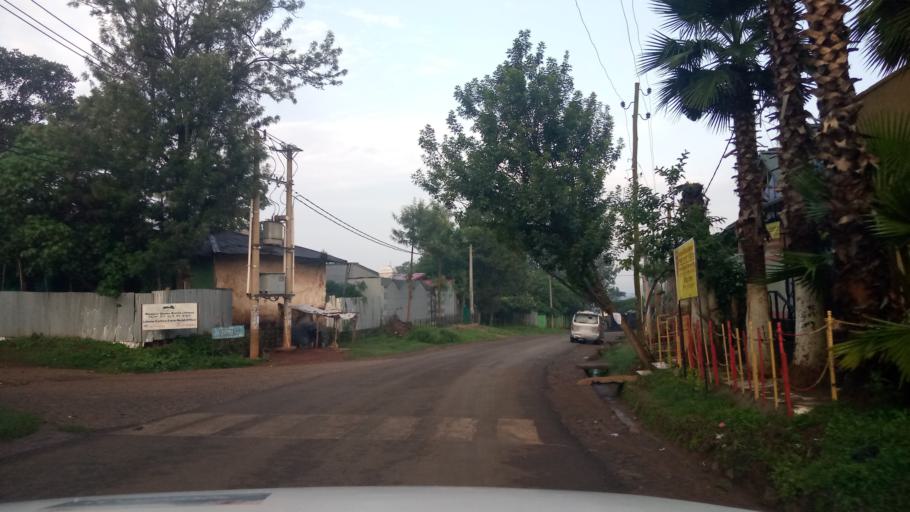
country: ET
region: Oromiya
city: Jima
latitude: 7.6766
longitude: 36.8399
